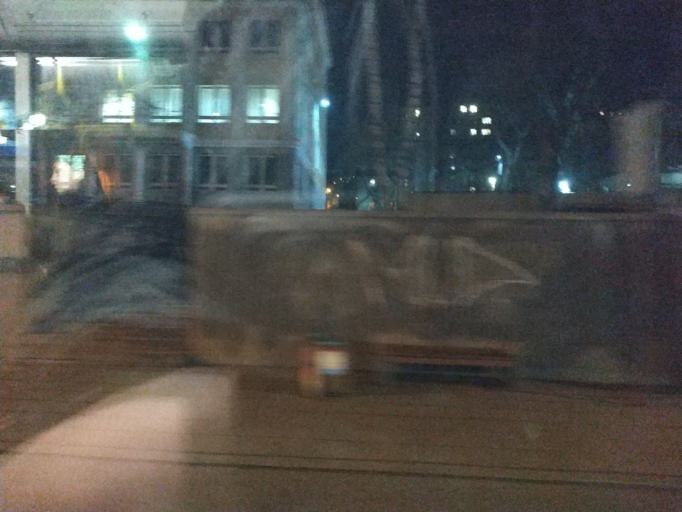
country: RU
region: Primorskiy
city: Vladivostok
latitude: 43.1230
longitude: 131.8882
